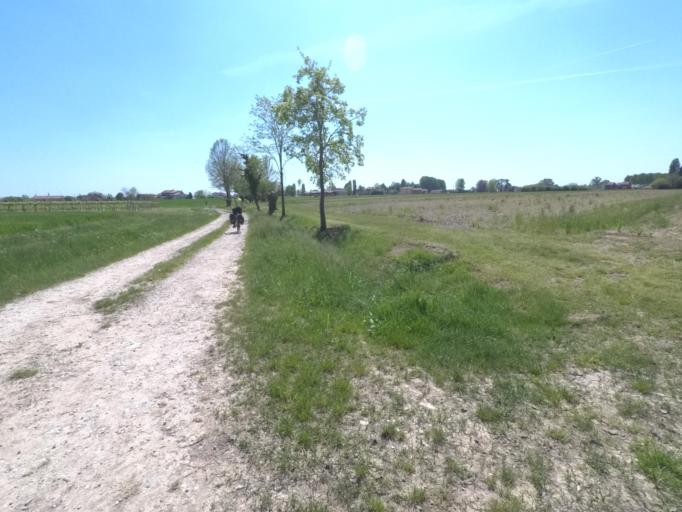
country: IT
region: Veneto
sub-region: Provincia di Treviso
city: Mansue
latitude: 45.8228
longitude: 12.5549
